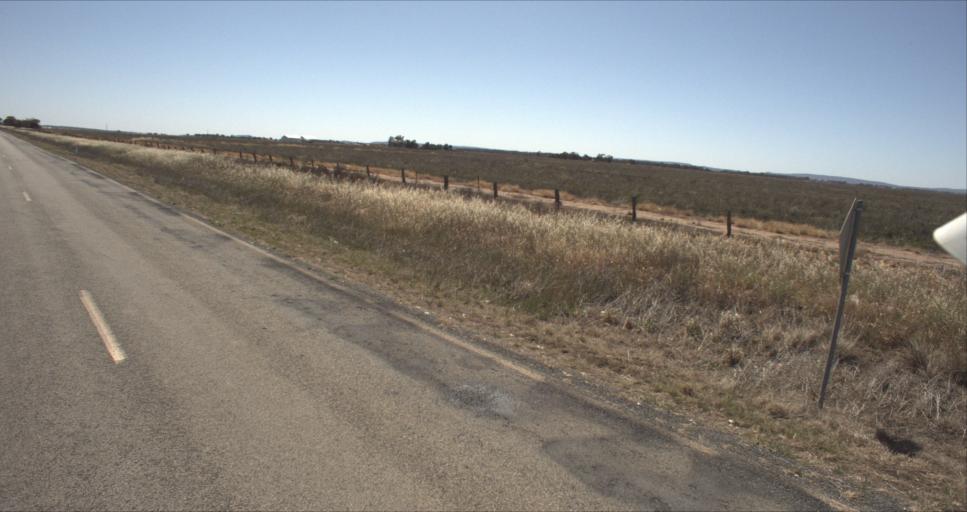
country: AU
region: New South Wales
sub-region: Leeton
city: Leeton
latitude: -34.5120
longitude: 146.2849
